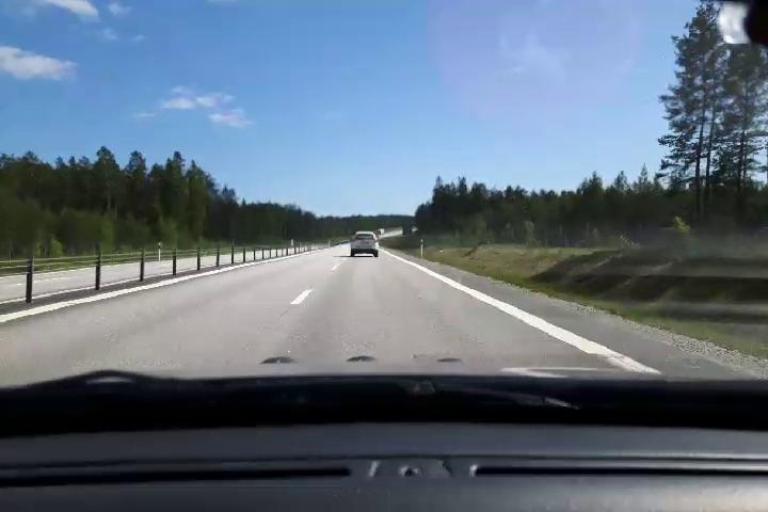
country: SE
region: Gaevleborg
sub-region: Hudiksvalls Kommun
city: Hudiksvall
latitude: 61.7021
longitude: 17.0538
